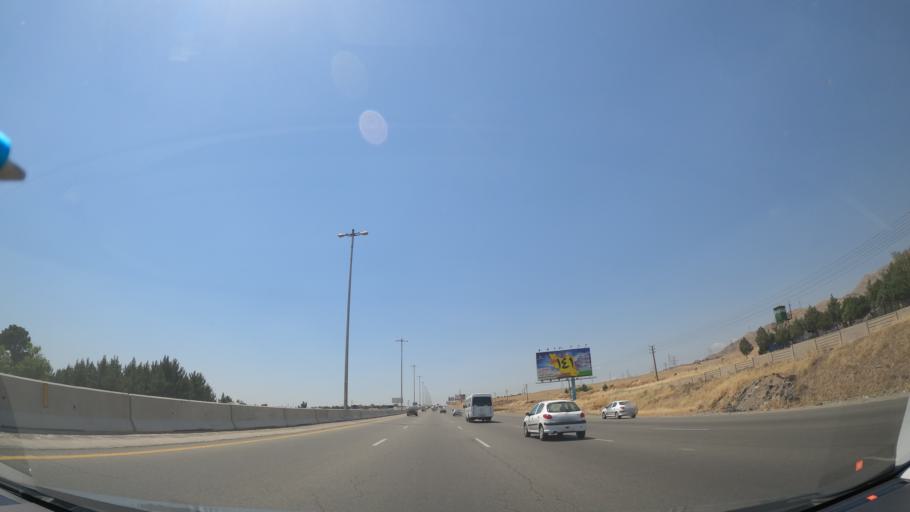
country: IR
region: Tehran
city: Shahr-e Qods
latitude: 35.7649
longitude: 51.0568
